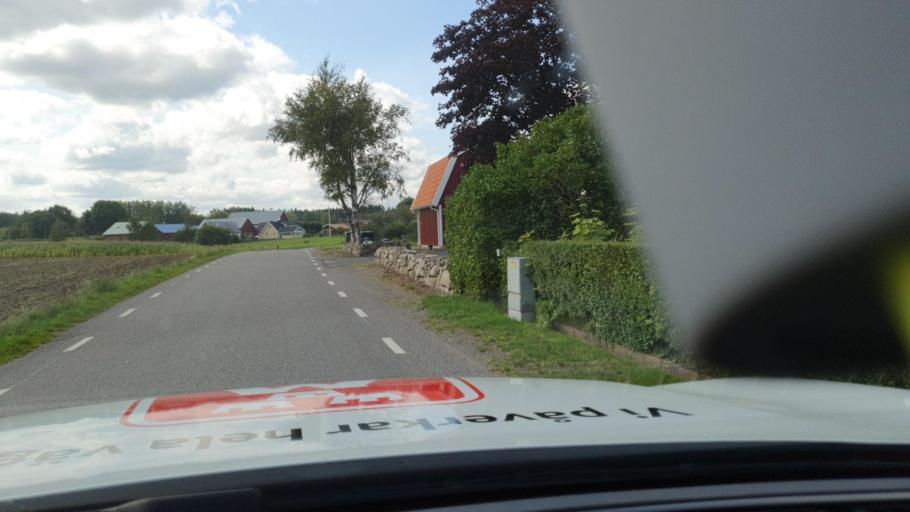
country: SE
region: Halland
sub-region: Laholms Kommun
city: Laholm
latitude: 56.4526
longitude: 13.1696
